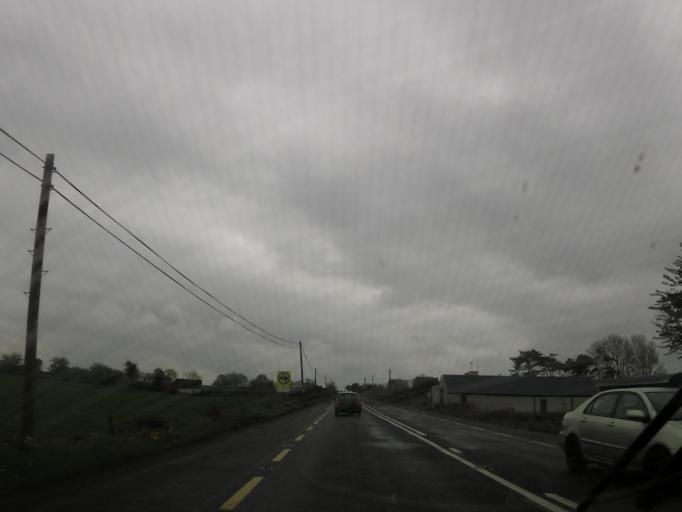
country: IE
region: Connaught
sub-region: County Galway
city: Tuam
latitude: 53.4385
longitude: -8.9052
